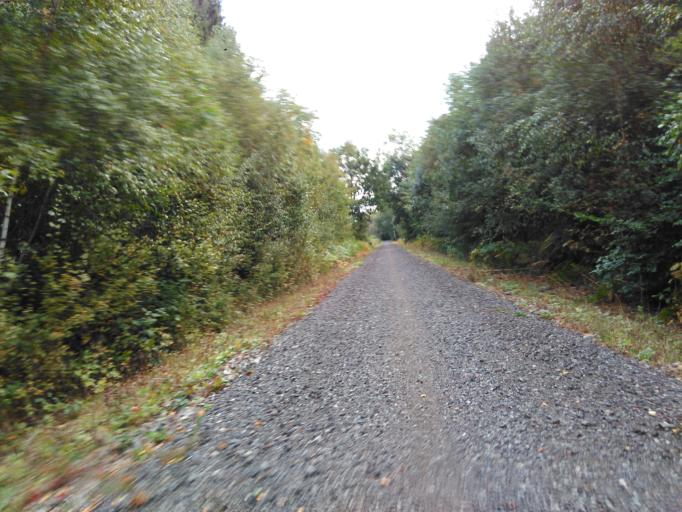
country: BE
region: Wallonia
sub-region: Province du Luxembourg
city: Neufchateau
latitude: 49.9062
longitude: 5.4730
